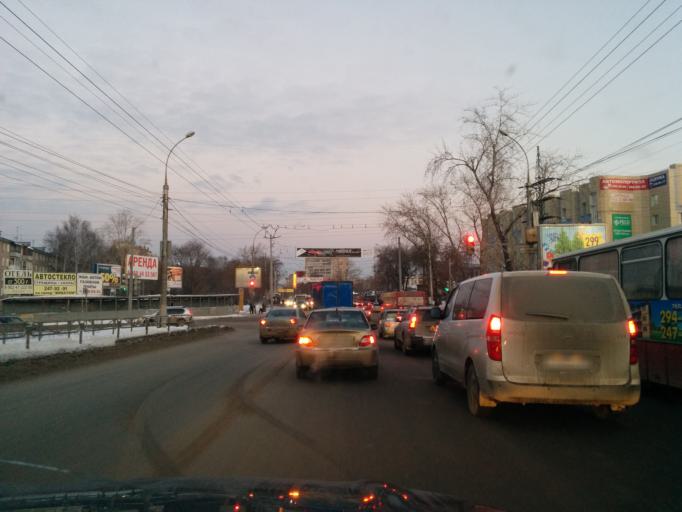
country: RU
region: Perm
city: Perm
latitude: 57.9941
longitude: 56.2106
